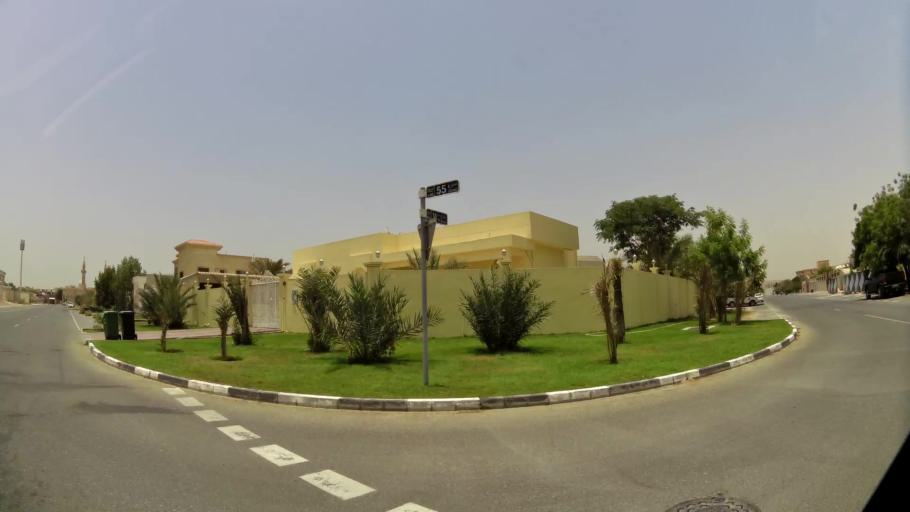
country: AE
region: Ash Shariqah
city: Sharjah
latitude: 25.2058
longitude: 55.3826
